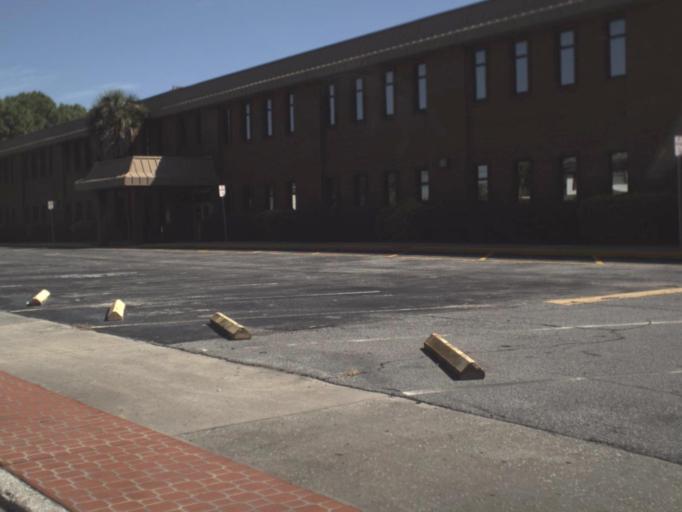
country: US
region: Florida
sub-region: Polk County
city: Auburndale
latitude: 28.0706
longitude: -81.7885
